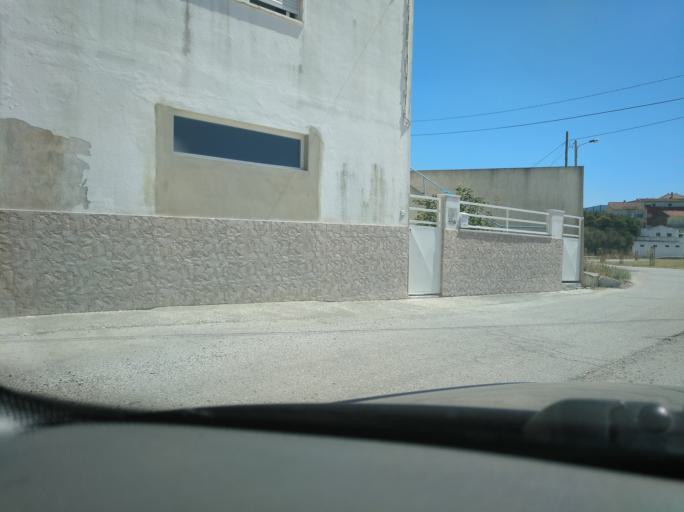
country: PT
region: Lisbon
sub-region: Loures
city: Apelacao
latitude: 38.8039
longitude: -9.1423
